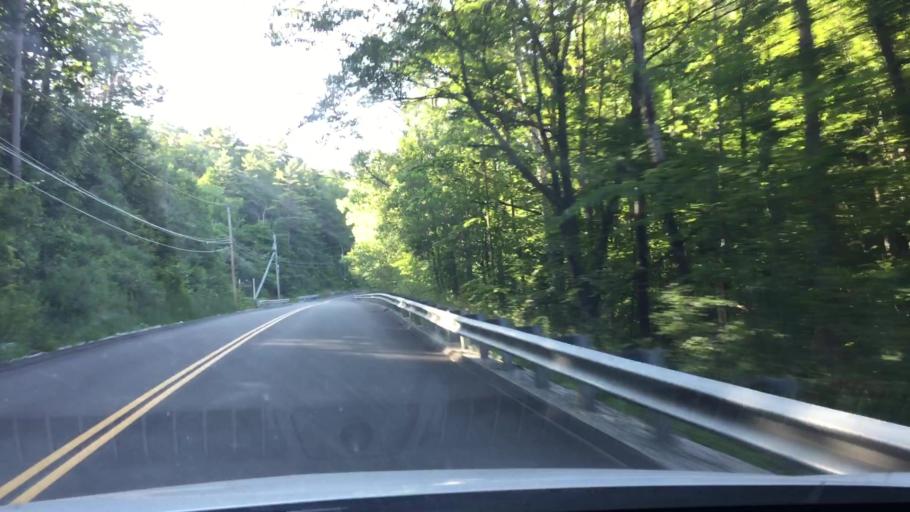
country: US
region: Massachusetts
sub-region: Berkshire County
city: Lee
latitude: 42.2921
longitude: -73.2172
